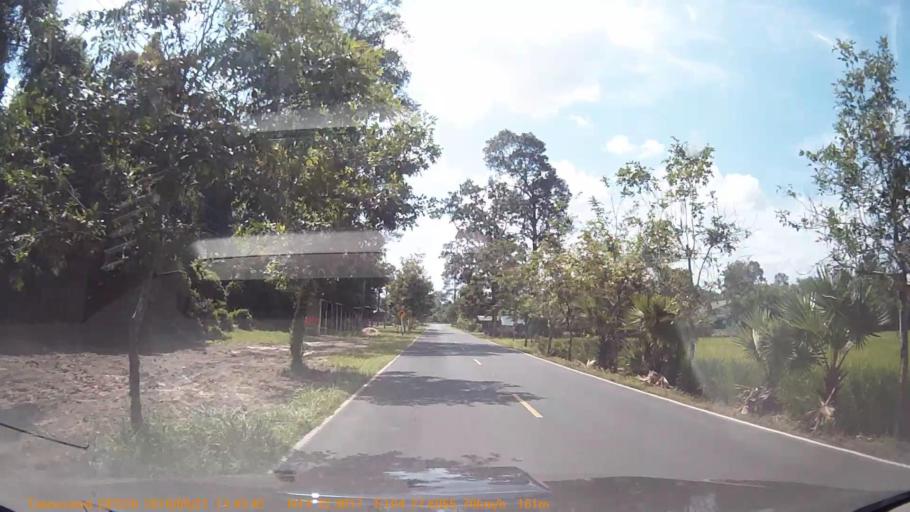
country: TH
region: Sisaket
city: Khun Han
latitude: 14.5485
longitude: 104.4595
